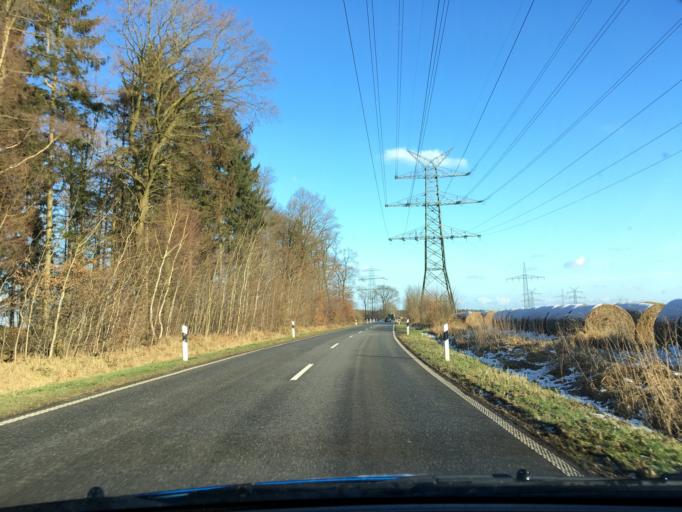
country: DE
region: Schleswig-Holstein
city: Wiershop
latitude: 53.4205
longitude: 10.4374
